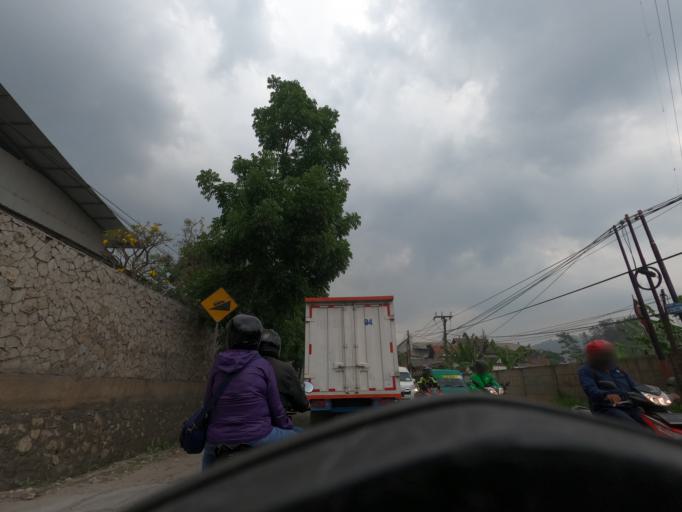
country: ID
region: West Java
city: Padalarang
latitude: -6.8323
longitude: 107.4597
